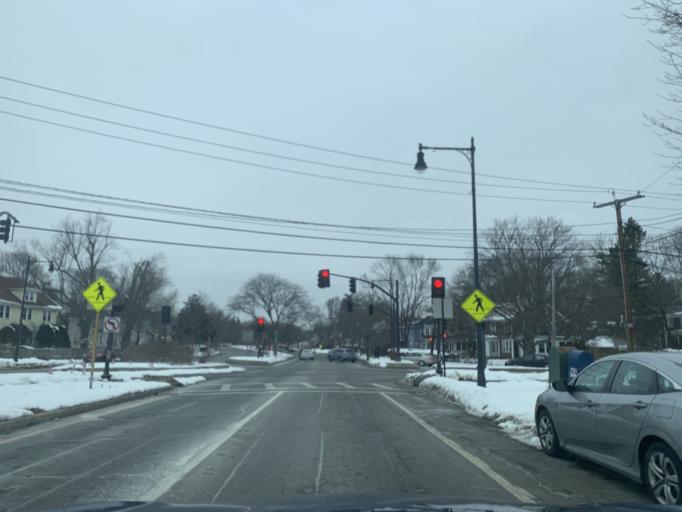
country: US
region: Massachusetts
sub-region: Norfolk County
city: Milton
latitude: 42.2621
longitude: -71.0935
